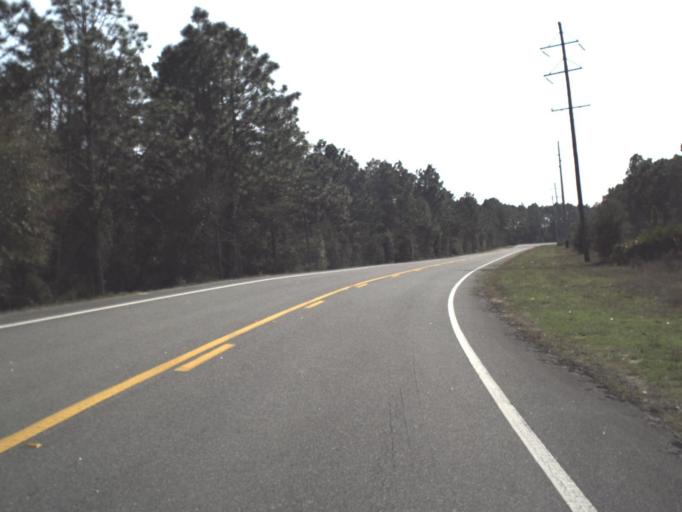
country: US
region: Florida
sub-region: Franklin County
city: Carrabelle
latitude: 29.9409
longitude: -84.5008
